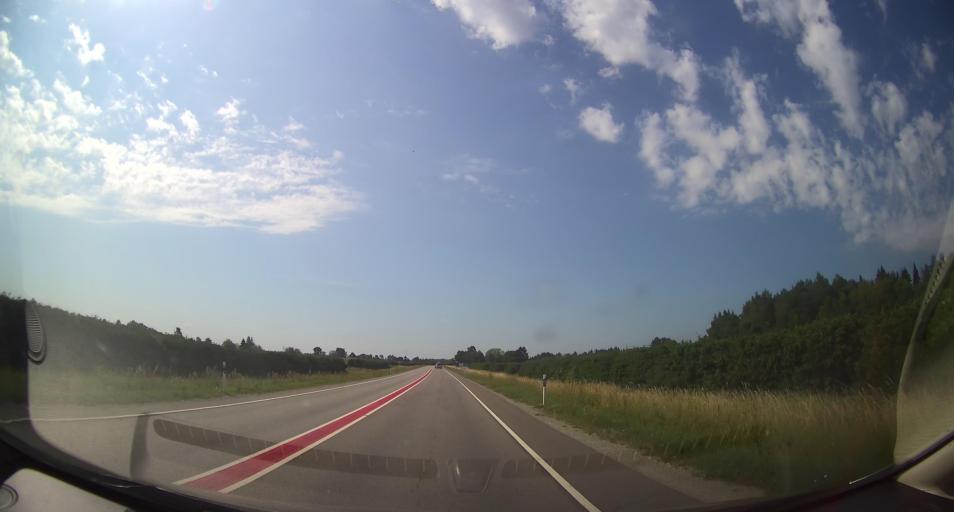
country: EE
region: Harju
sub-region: Kiili vald
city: Kiili
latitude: 59.3041
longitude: 24.7484
